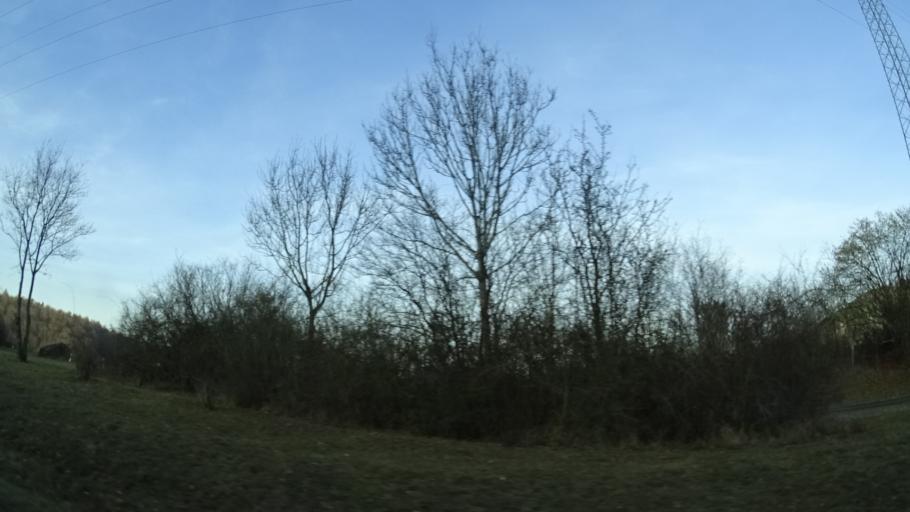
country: DE
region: Hesse
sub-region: Regierungsbezirk Darmstadt
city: Schluchtern
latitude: 50.3307
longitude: 9.5834
